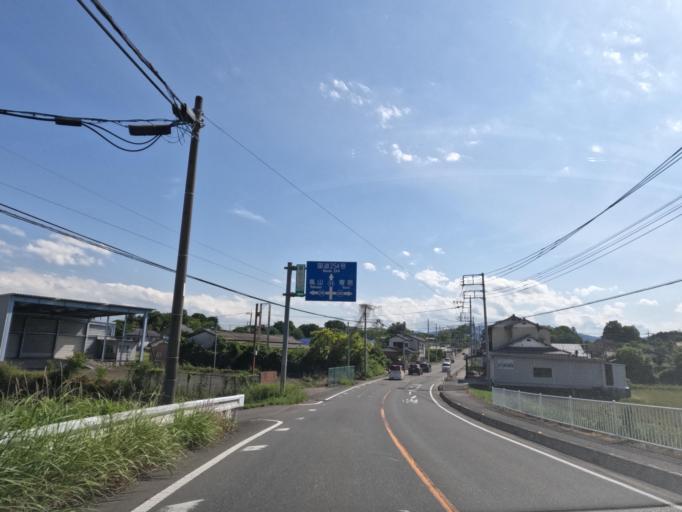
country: JP
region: Saitama
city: Ogawa
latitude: 36.0804
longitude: 139.2907
